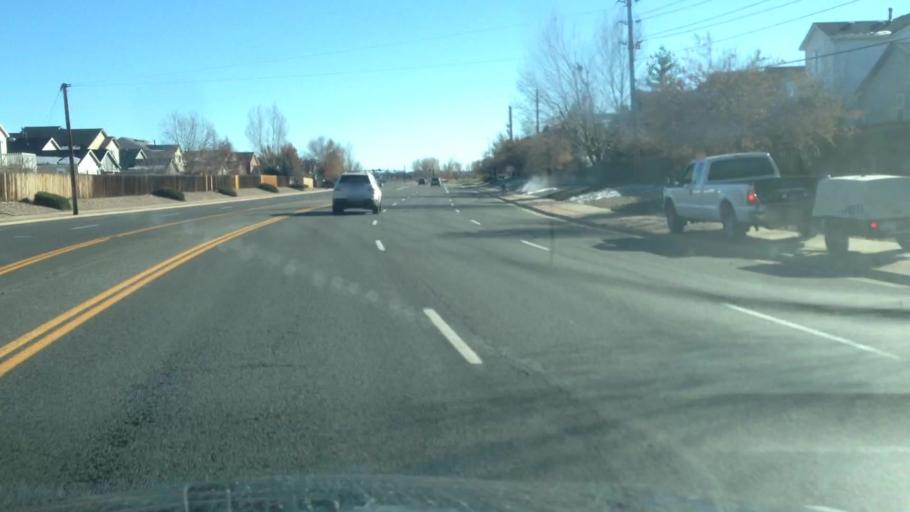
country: US
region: Colorado
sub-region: Douglas County
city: Stonegate
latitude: 39.5588
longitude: -104.7958
